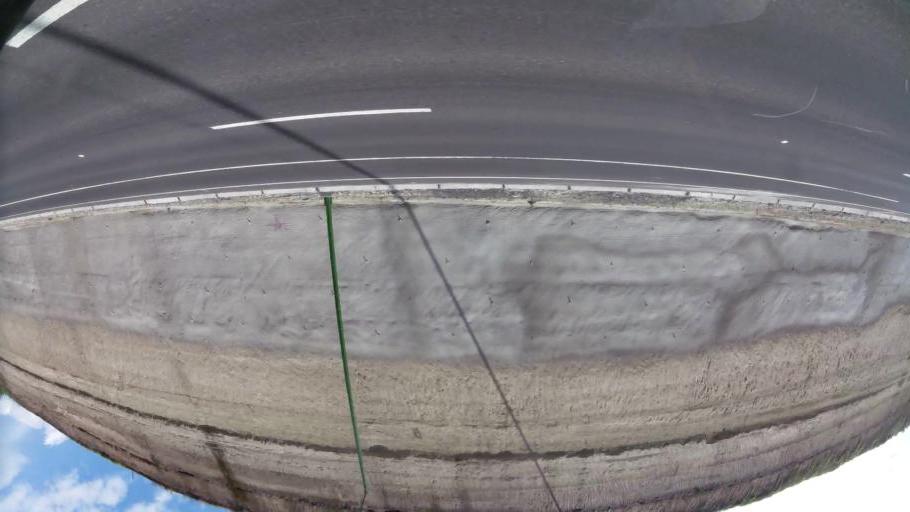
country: EC
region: Pichincha
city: Sangolqui
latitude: -0.2105
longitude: -78.3318
